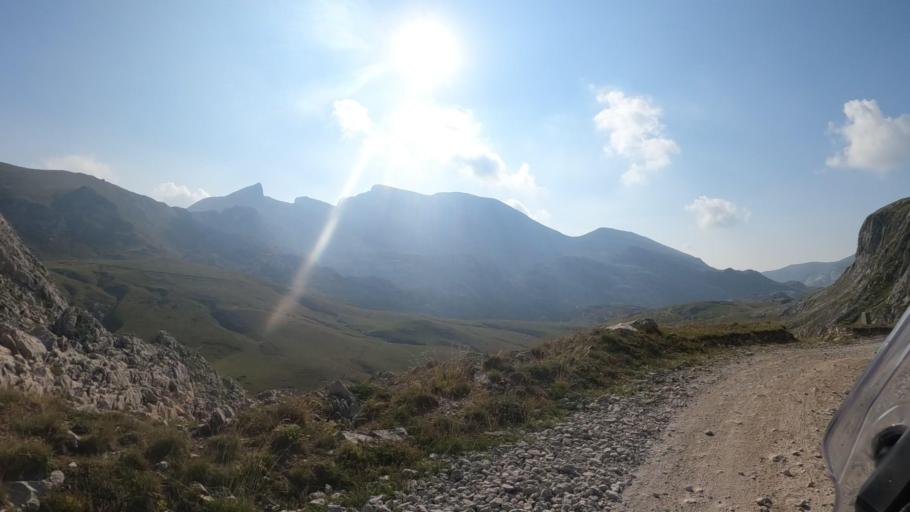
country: IT
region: Piedmont
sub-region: Provincia di Cuneo
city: Limone Piemonte
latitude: 44.1711
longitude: 7.6560
